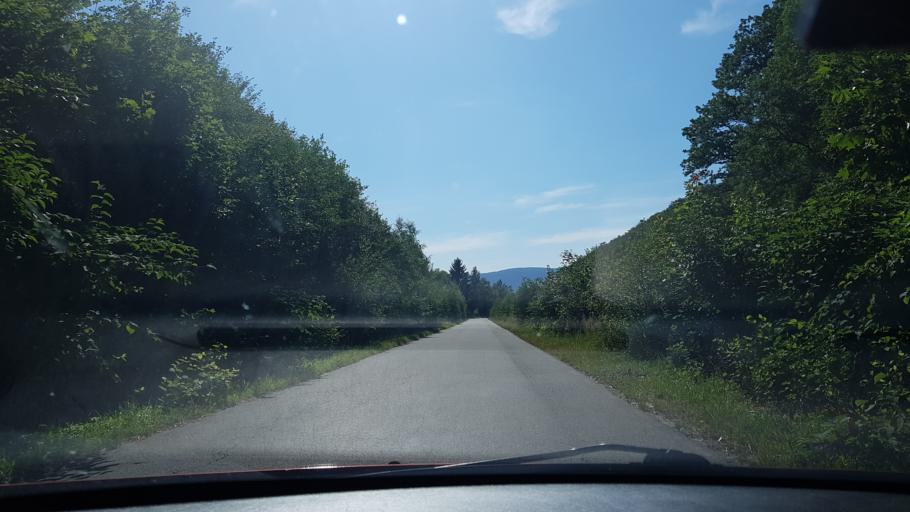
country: PL
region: Lower Silesian Voivodeship
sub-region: Powiat klodzki
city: Miedzylesie
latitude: 50.2329
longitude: 16.7379
